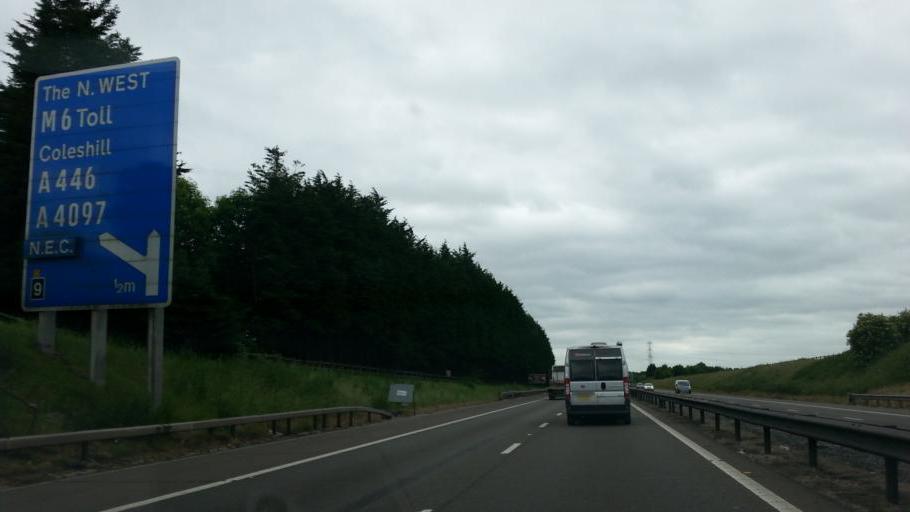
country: GB
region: England
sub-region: Warwickshire
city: Curdworth
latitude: 52.5530
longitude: -1.7127
